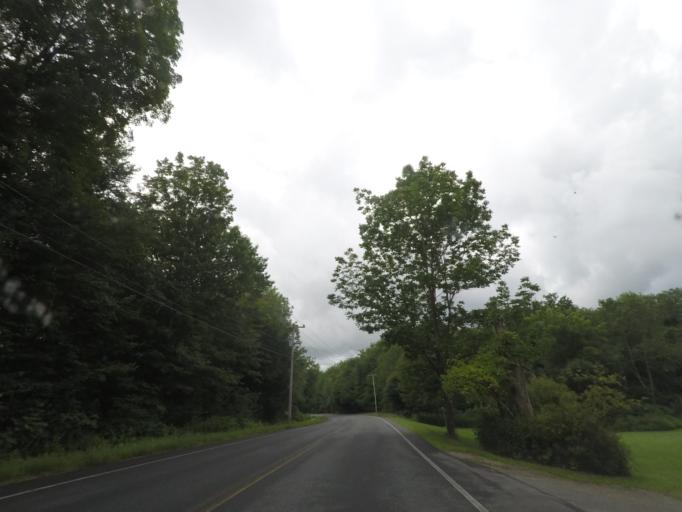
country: US
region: Massachusetts
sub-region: Berkshire County
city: Lanesborough
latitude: 42.5644
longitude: -73.2842
